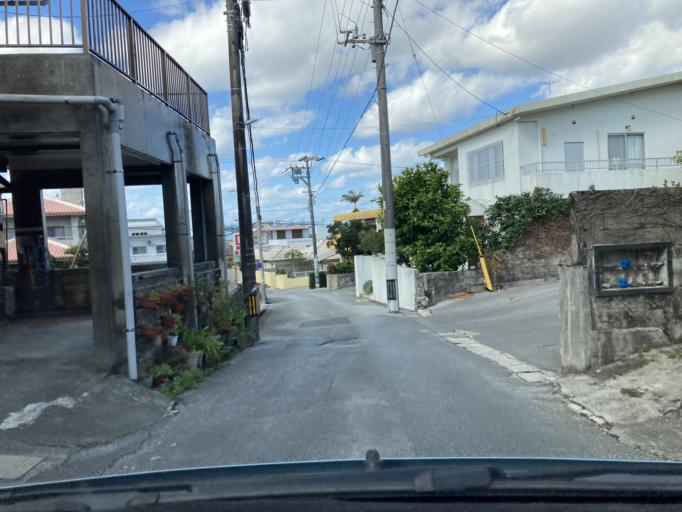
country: JP
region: Okinawa
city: Okinawa
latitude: 26.3268
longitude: 127.7931
